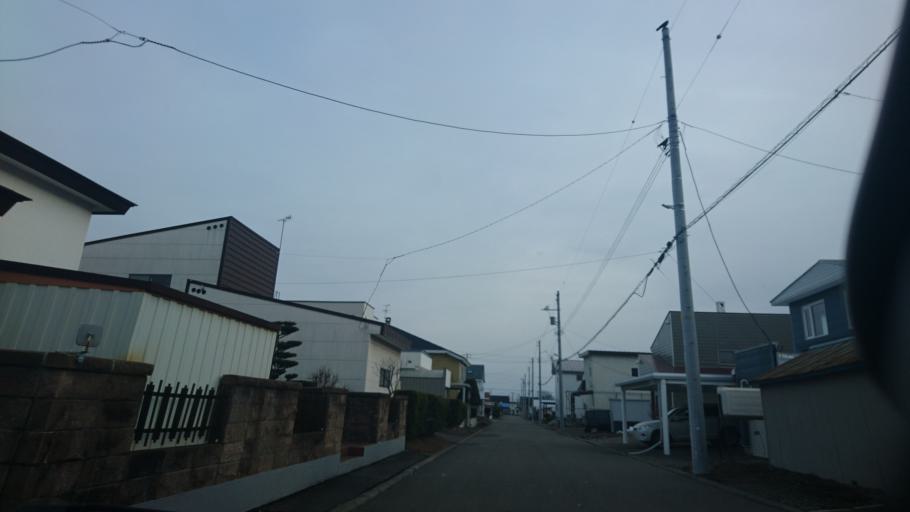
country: JP
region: Hokkaido
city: Otofuke
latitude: 42.9957
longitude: 143.1908
